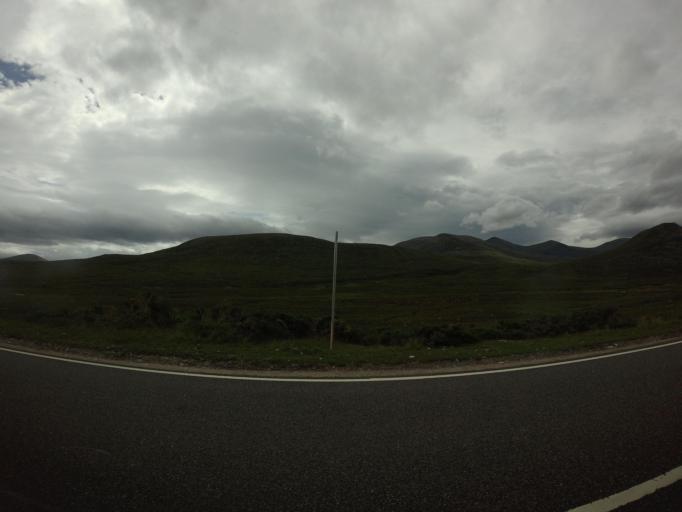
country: GB
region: Scotland
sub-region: Highland
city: Ullapool
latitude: 57.7369
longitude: -4.9514
